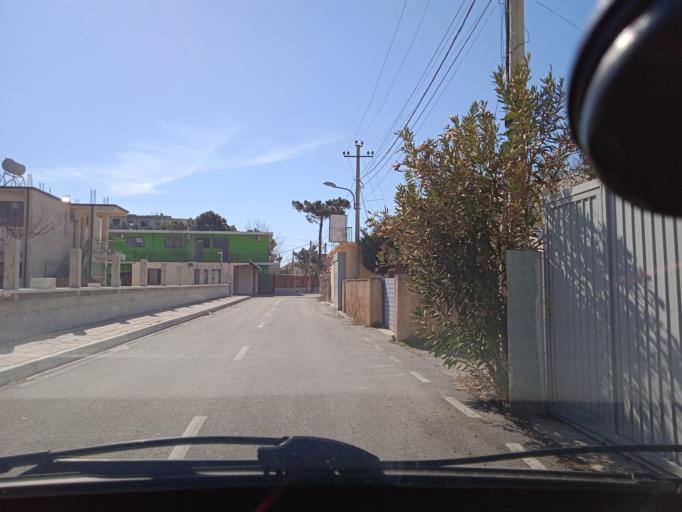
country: AL
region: Shkoder
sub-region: Rrethi i Shkodres
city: Velipoje
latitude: 41.8646
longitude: 19.4121
